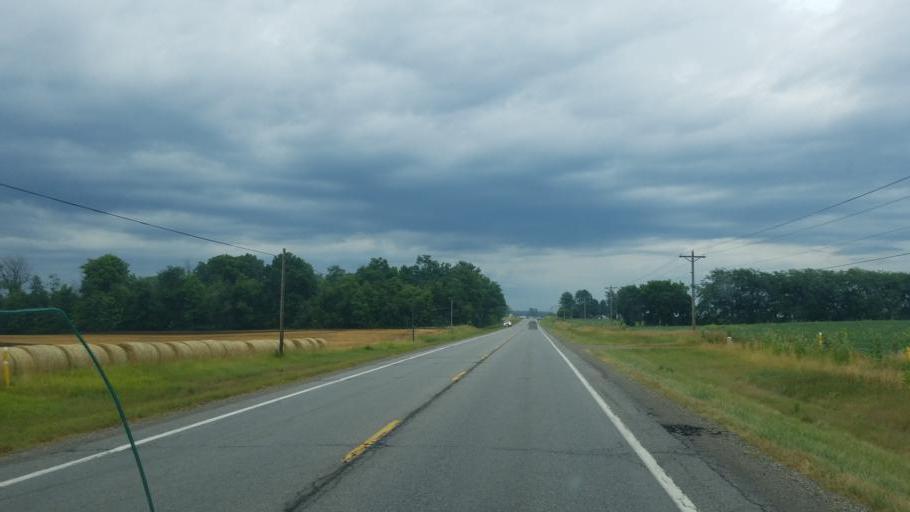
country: US
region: Ohio
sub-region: Williams County
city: Edgerton
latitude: 41.4481
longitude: -84.7030
